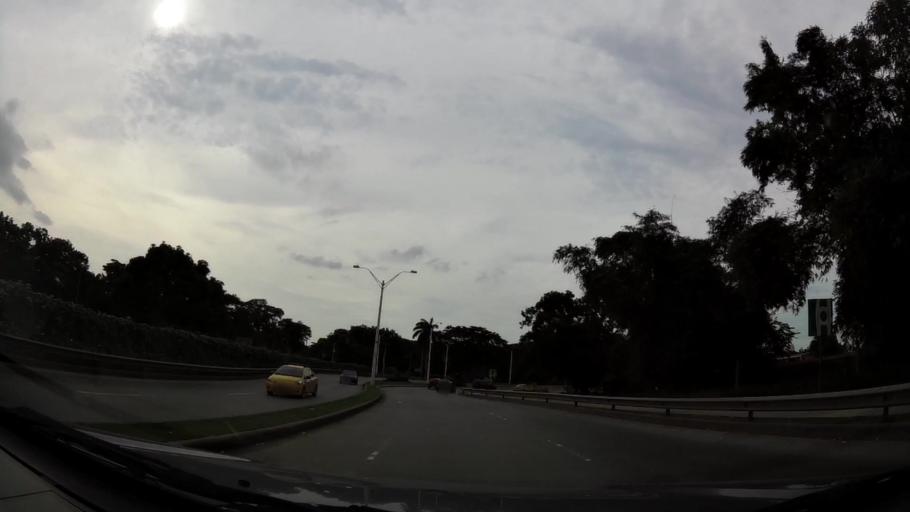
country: PA
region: Panama
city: Panama
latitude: 9.0094
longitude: -79.4867
